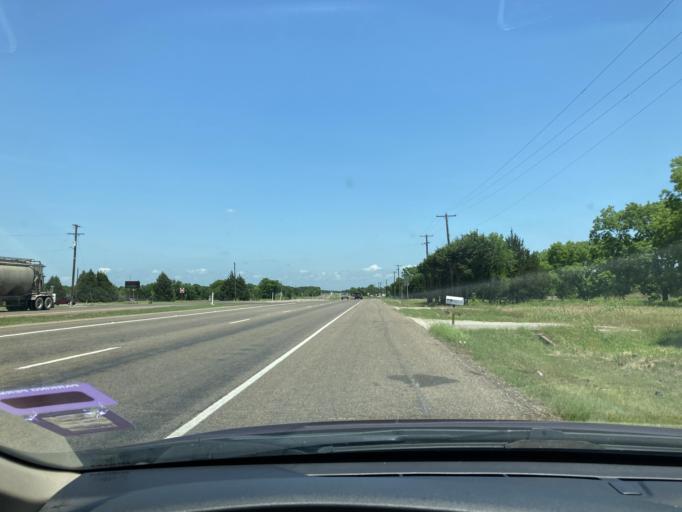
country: US
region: Texas
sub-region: Navarro County
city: Kerens
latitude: 32.1345
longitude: -96.2198
